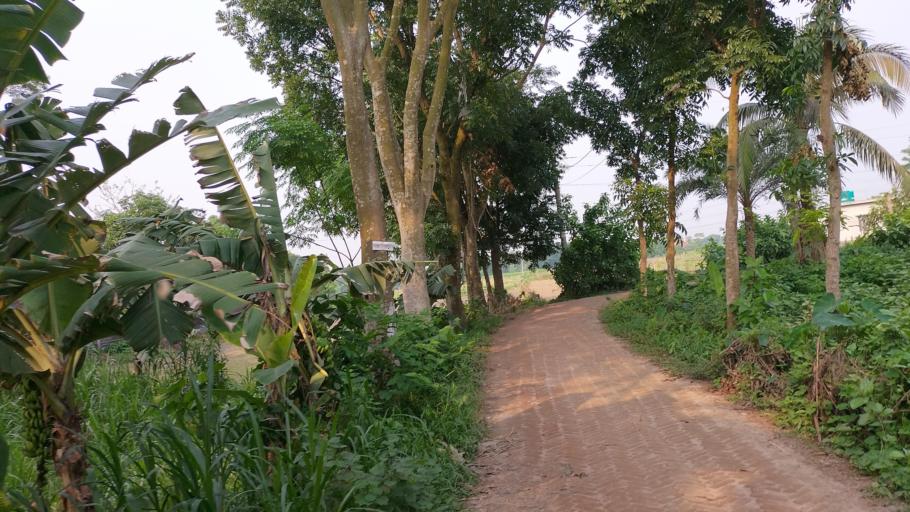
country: BD
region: Dhaka
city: Azimpur
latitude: 23.6722
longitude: 90.3129
